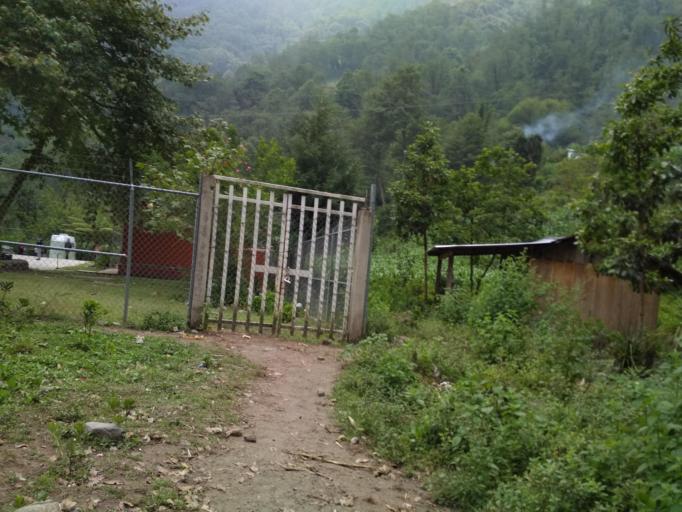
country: MX
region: Veracruz
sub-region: La Perla
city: Metlac Hernandez (Metlac Primero)
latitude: 18.9896
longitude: -97.1195
